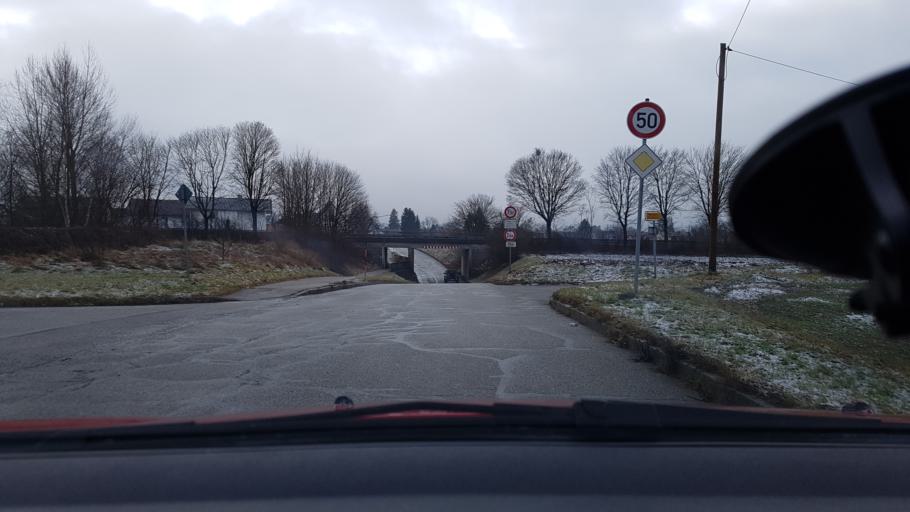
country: DE
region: Bavaria
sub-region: Upper Bavaria
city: Altoetting
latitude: 48.2366
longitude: 12.6698
